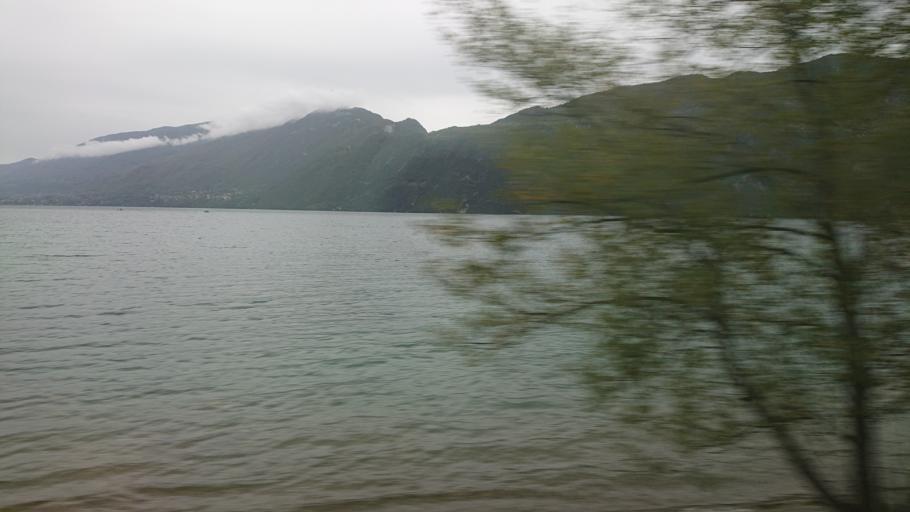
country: FR
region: Rhone-Alpes
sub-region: Departement de la Savoie
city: Brison-Saint-Innocent
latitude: 45.7151
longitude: 5.8881
